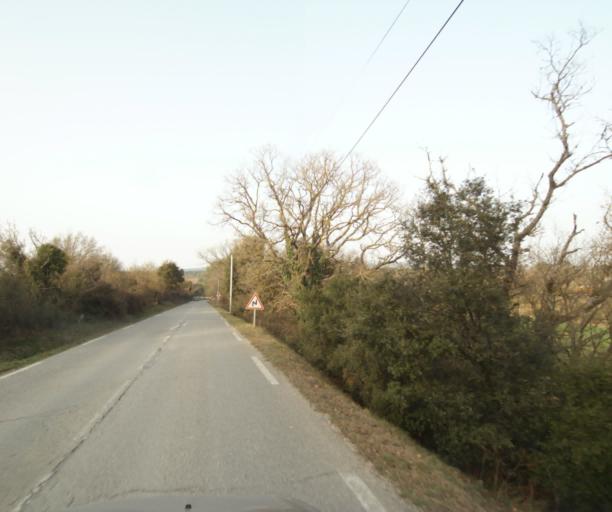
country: FR
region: Provence-Alpes-Cote d'Azur
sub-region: Departement des Bouches-du-Rhone
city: Eguilles
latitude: 43.5813
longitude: 5.3656
